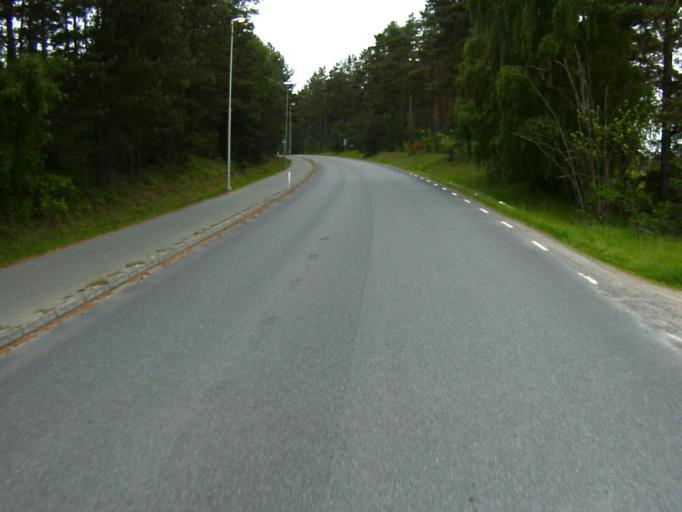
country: SE
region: Skane
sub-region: Kristianstads Kommun
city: Ahus
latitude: 55.9121
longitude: 14.2764
